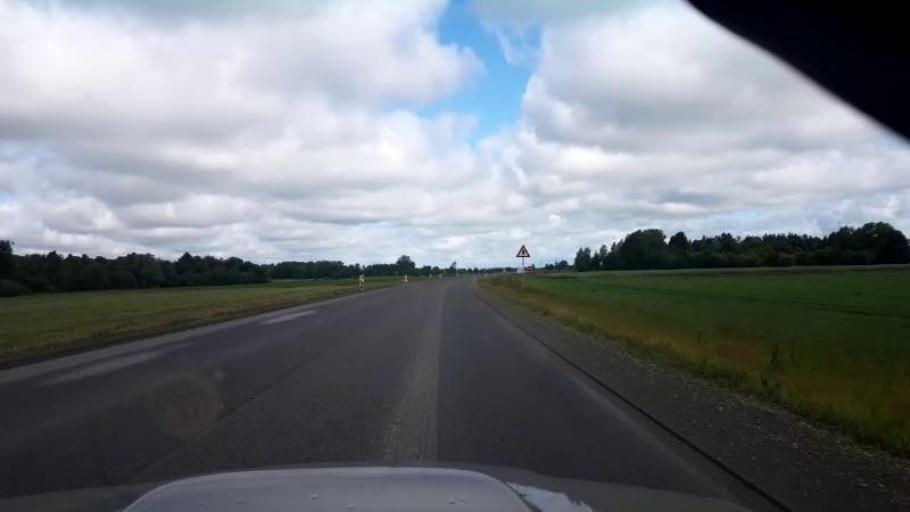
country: LV
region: Bauskas Rajons
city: Bauska
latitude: 56.2967
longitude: 24.3459
